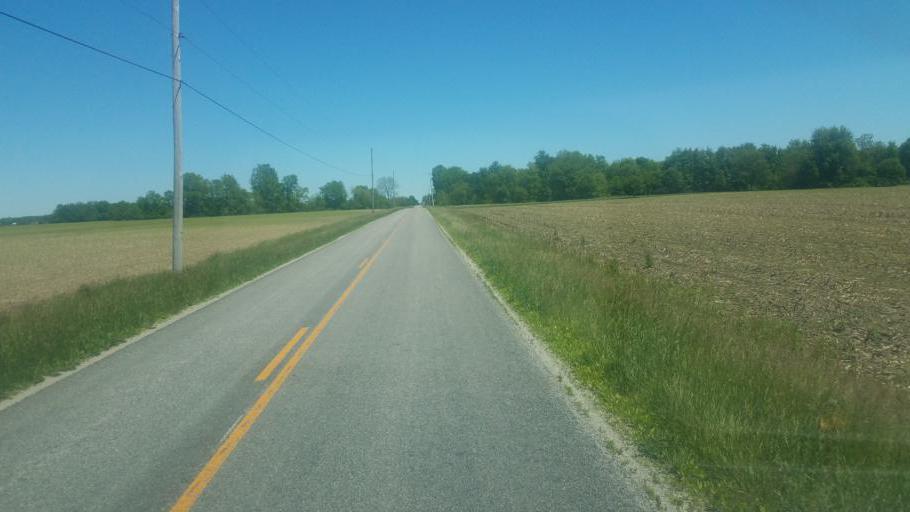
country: US
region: Ohio
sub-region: Shelby County
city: Sidney
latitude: 40.2135
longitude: -84.1529
